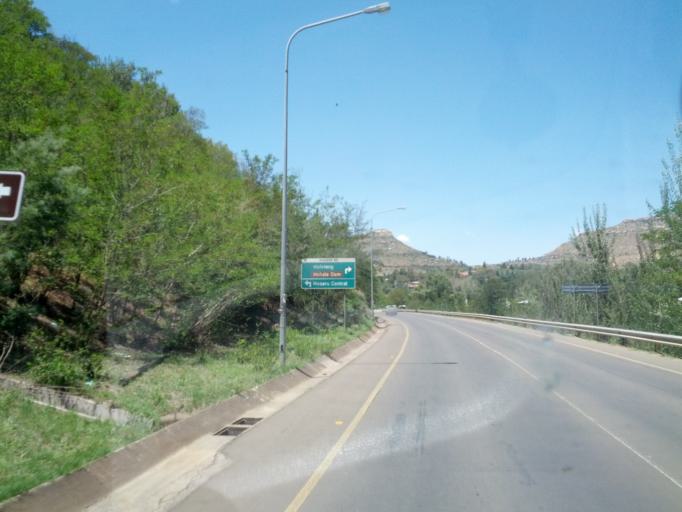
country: LS
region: Maseru
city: Maseru
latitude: -29.3170
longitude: 27.4721
